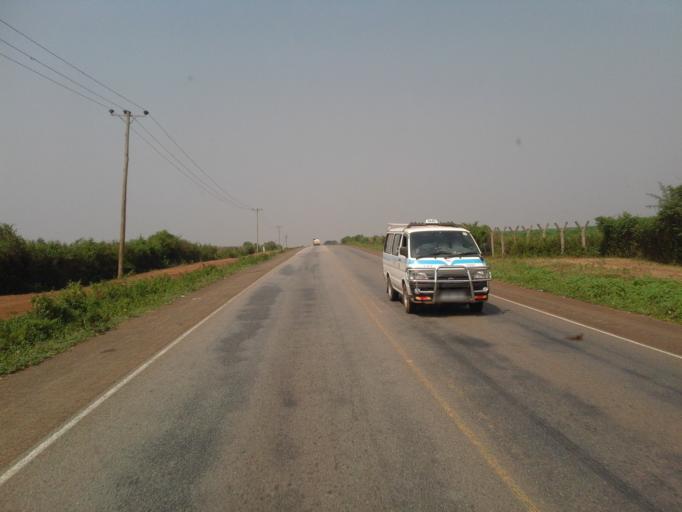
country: UG
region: Eastern Region
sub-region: Iganga District
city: Iganga
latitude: 0.6295
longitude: 33.5359
